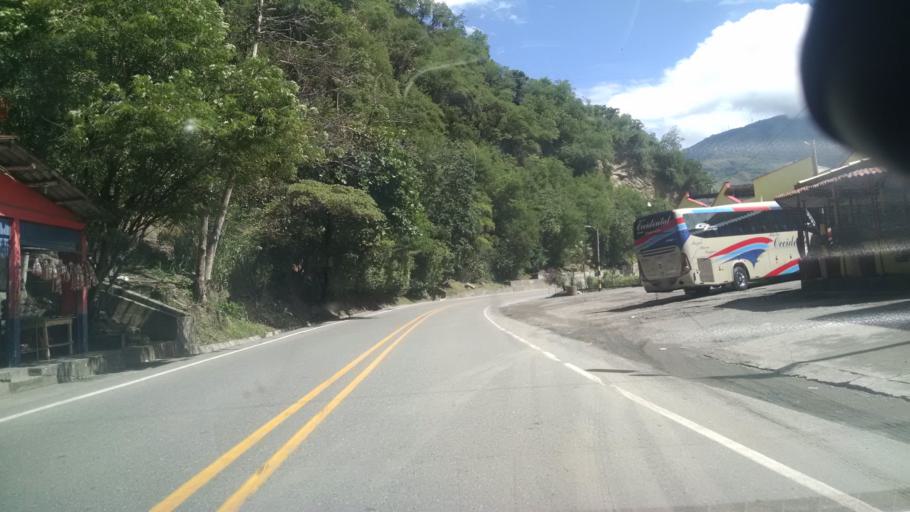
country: CO
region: Caldas
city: Supia
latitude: 5.3823
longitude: -75.6060
